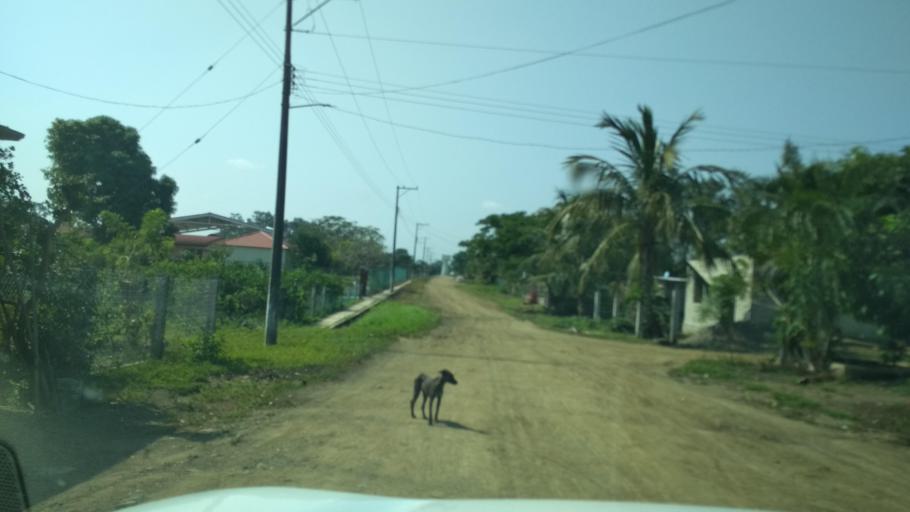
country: MX
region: Puebla
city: San Jose Acateno
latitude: 20.1958
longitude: -97.1849
